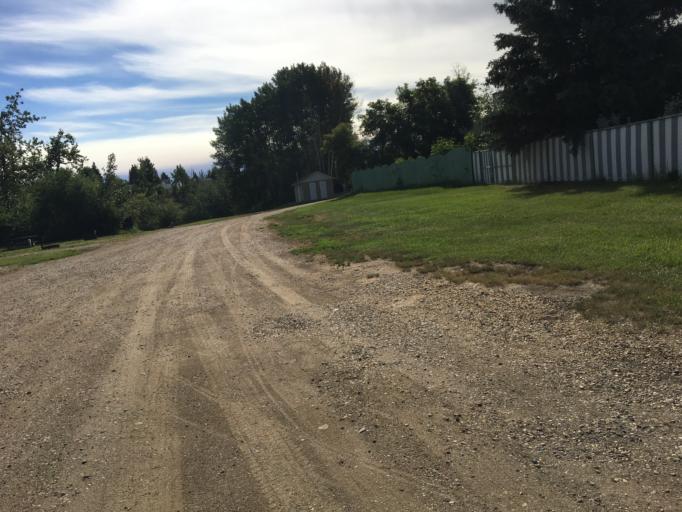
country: CA
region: Alberta
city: Manning
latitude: 56.9247
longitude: -117.6336
